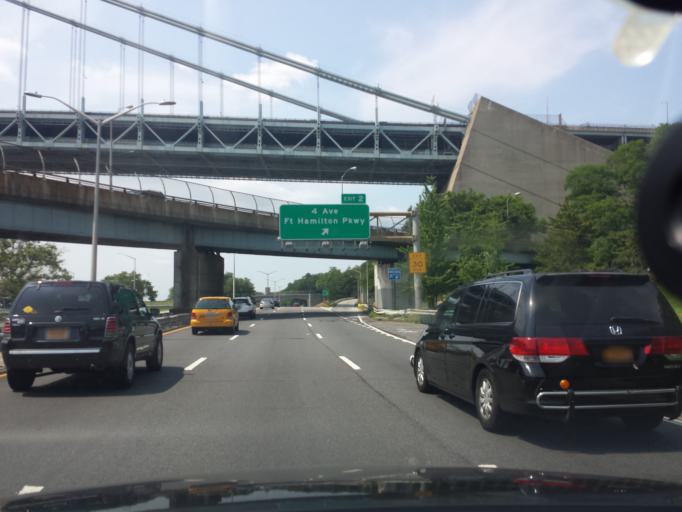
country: US
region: New York
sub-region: Kings County
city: Bensonhurst
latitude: 40.6083
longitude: -74.0342
